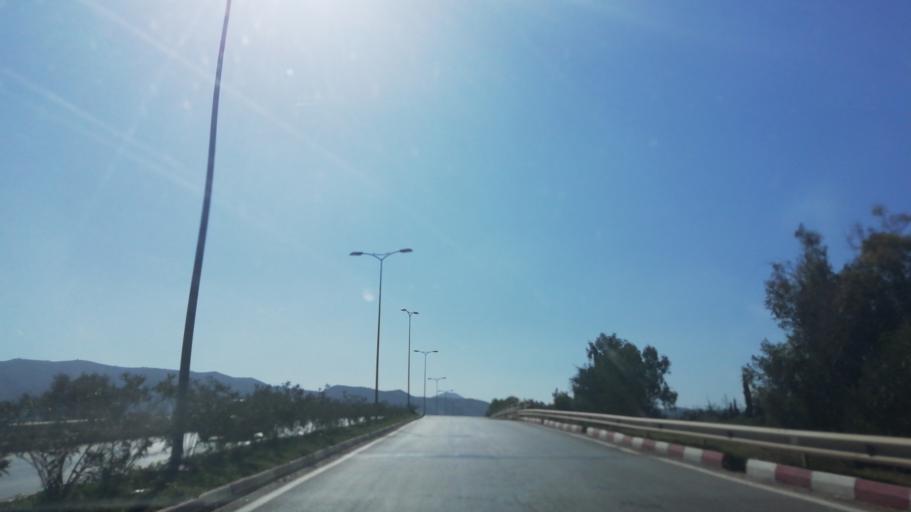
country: DZ
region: Mascara
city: Sig
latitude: 35.5401
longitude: -0.2042
